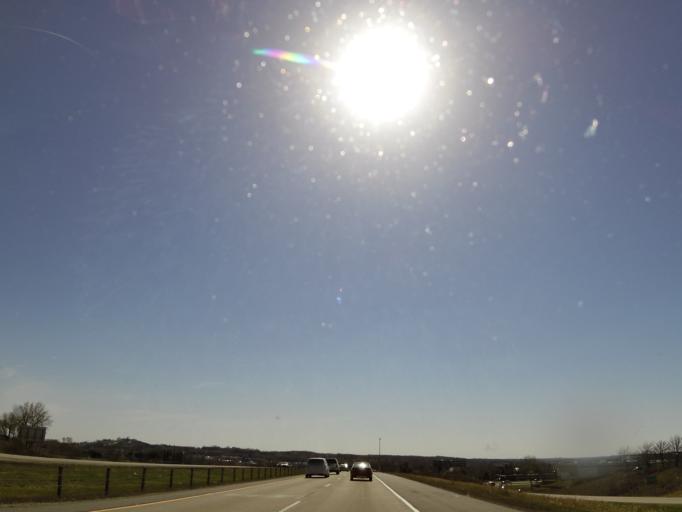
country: US
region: Minnesota
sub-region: Dakota County
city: Burnsville
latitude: 44.7454
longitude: -93.2744
